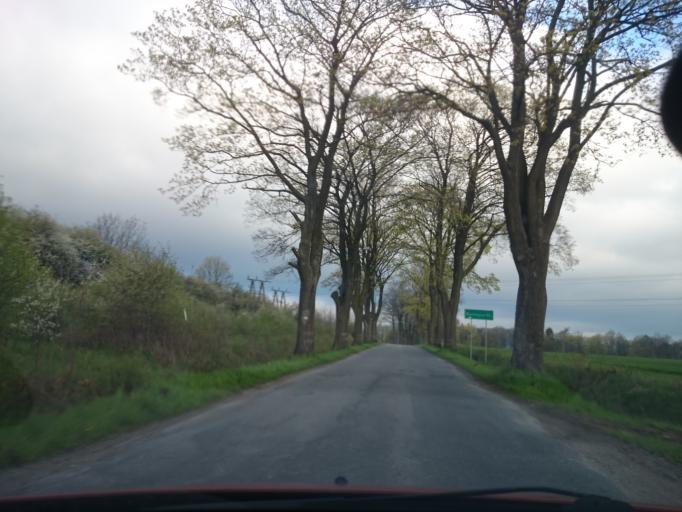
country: PL
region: Lower Silesian Voivodeship
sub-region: Powiat klodzki
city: Bystrzyca Klodzka
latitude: 50.2918
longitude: 16.6616
